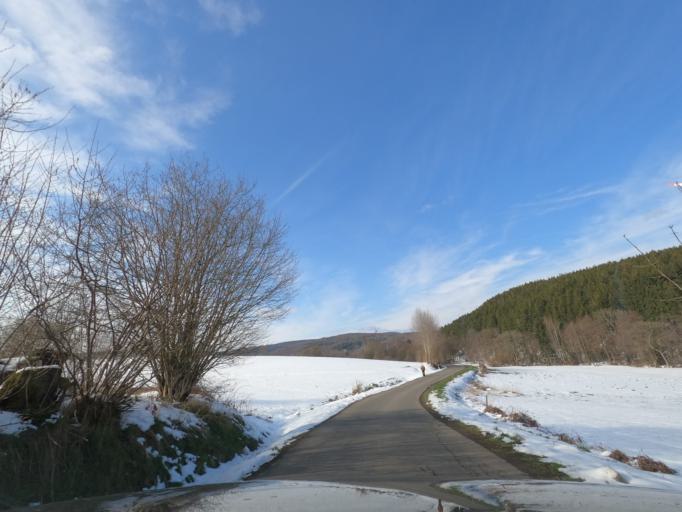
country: DE
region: North Rhine-Westphalia
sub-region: Regierungsbezirk Arnsberg
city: Herscheid
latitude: 51.1179
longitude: 7.7764
